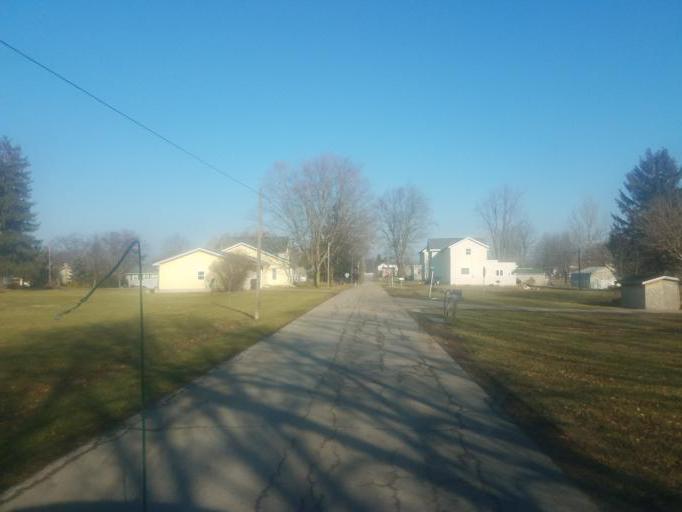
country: US
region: Ohio
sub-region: Seneca County
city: Tiffin
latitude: 41.0485
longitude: -83.0106
